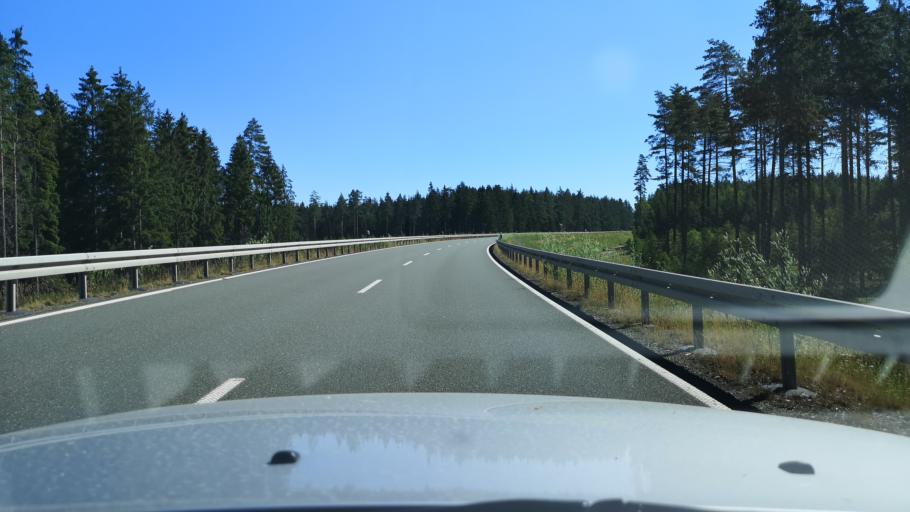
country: DE
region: Thuringia
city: Birkenhugel
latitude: 50.4346
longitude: 11.7386
